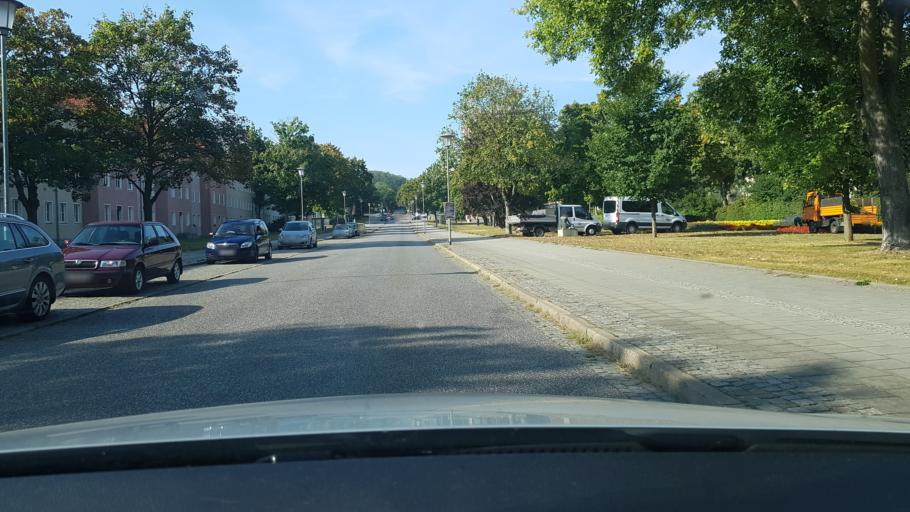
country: DE
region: Brandenburg
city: Eisenhuettenstadt
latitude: 52.1481
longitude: 14.6217
